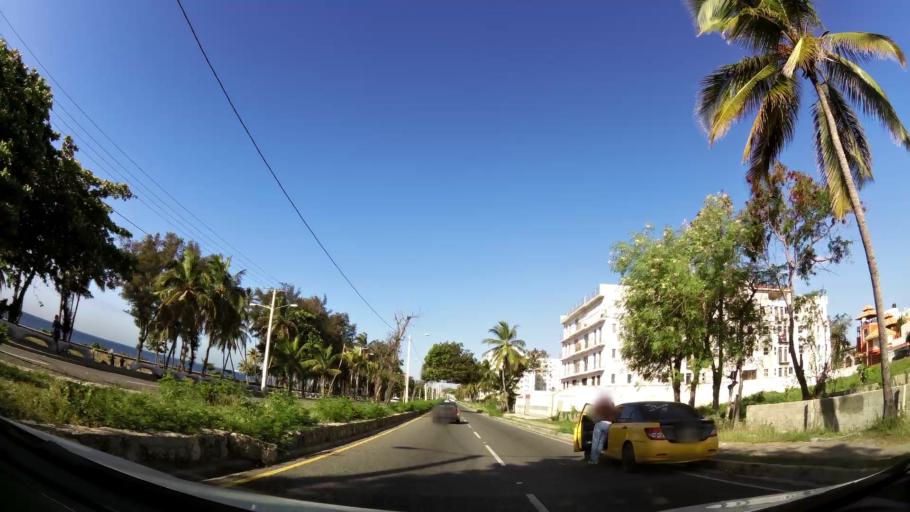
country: DO
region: Santo Domingo
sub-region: Santo Domingo
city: Santo Domingo Este
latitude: 18.4695
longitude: -69.8594
